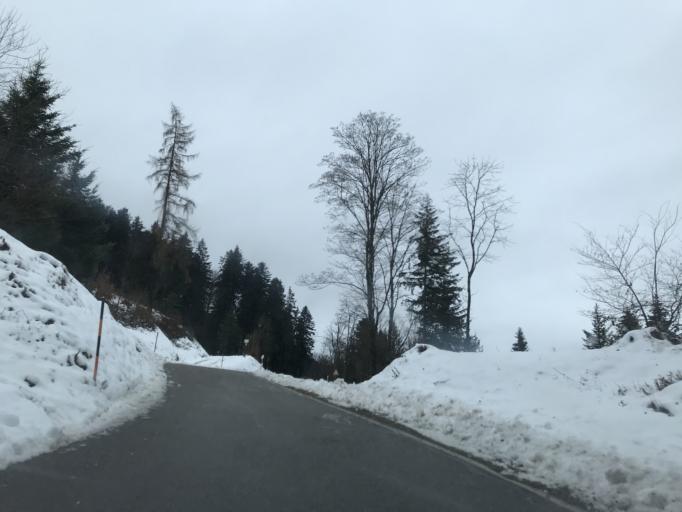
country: DE
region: Baden-Wuerttemberg
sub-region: Freiburg Region
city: Hasel
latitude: 47.6828
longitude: 7.8923
